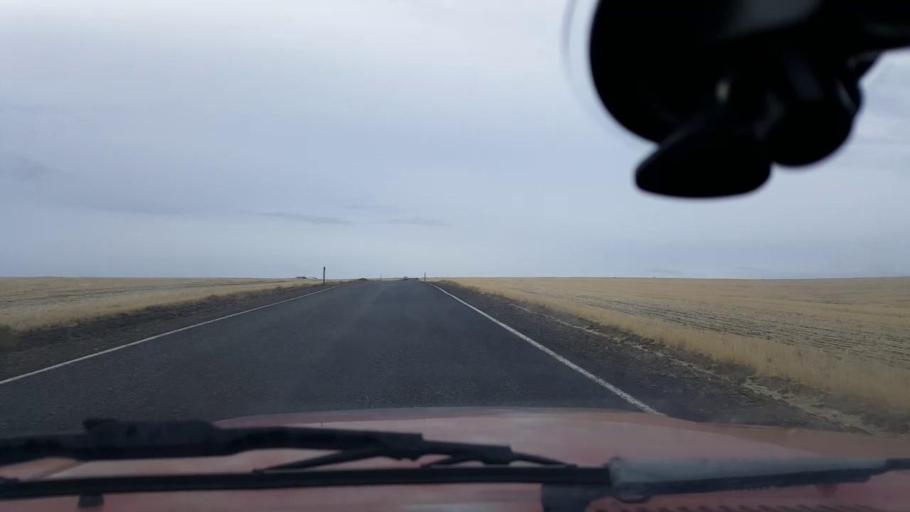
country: US
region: Washington
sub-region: Asotin County
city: Clarkston Heights-Vineland
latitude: 46.3438
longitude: -117.2645
